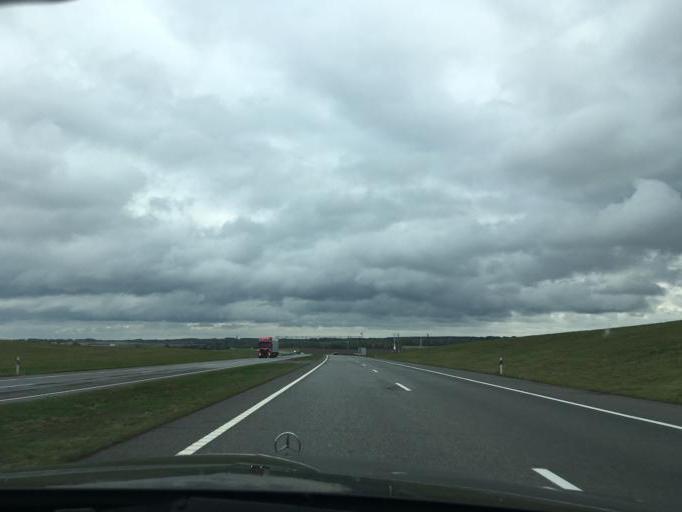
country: BY
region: Vitebsk
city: Kokhanava
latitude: 54.4751
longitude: 29.8625
